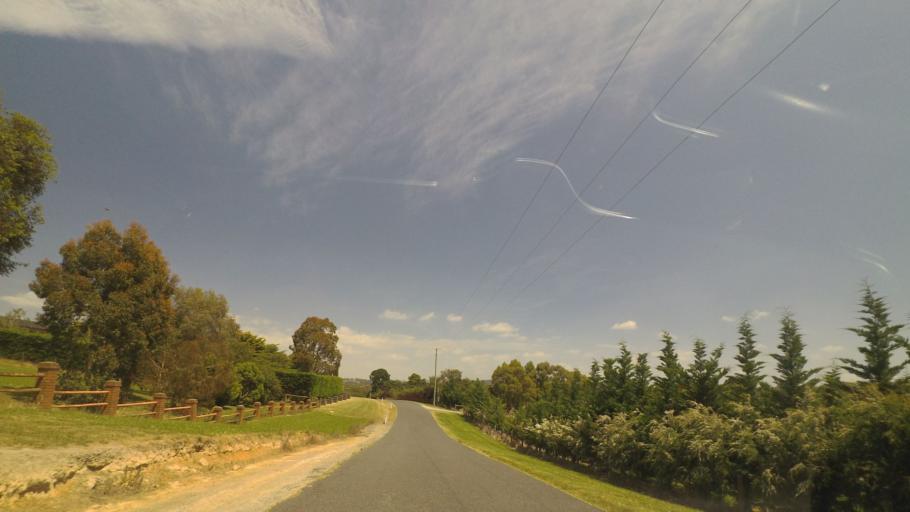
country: AU
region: Victoria
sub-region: Yarra Ranges
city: Chirnside Park
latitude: -37.7524
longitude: 145.3008
